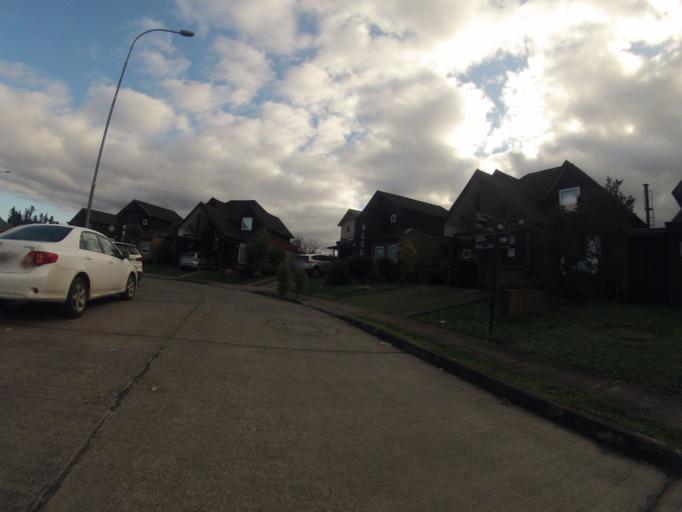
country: CL
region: Araucania
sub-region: Provincia de Cautin
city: Temuco
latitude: -38.7351
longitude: -72.6482
